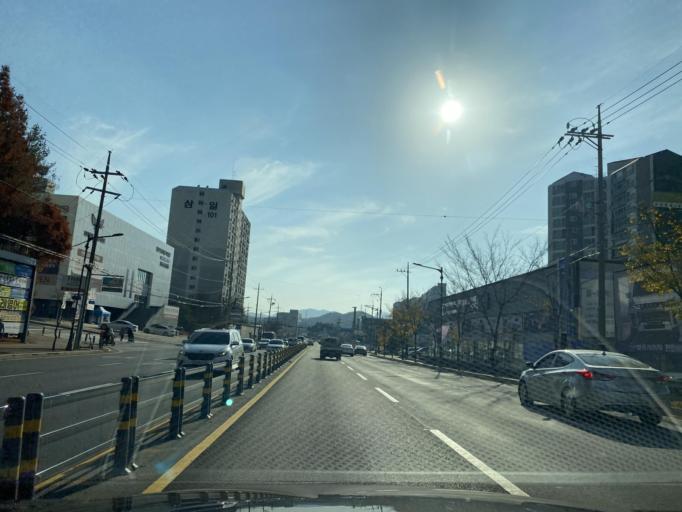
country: KR
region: Chungcheongnam-do
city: Cheonan
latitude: 36.7914
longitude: 127.1203
